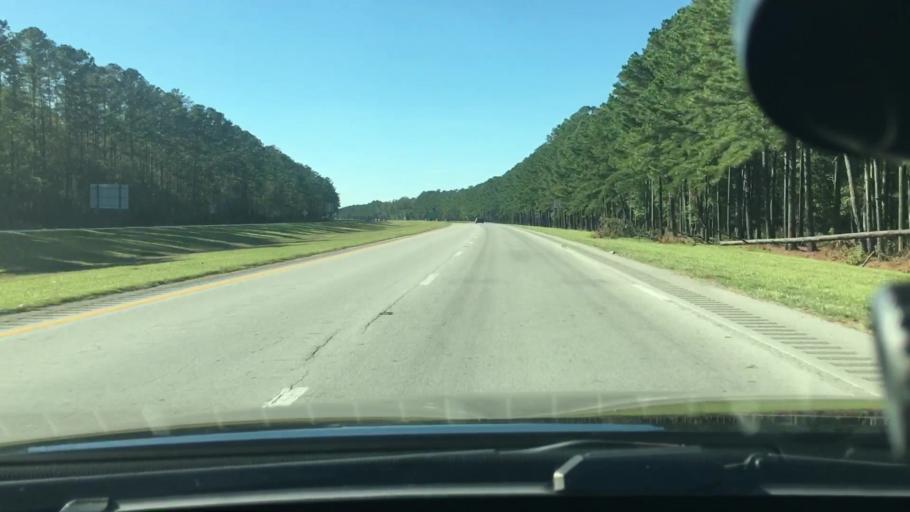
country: US
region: North Carolina
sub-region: Craven County
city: Trent Woods
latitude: 35.1175
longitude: -77.1048
